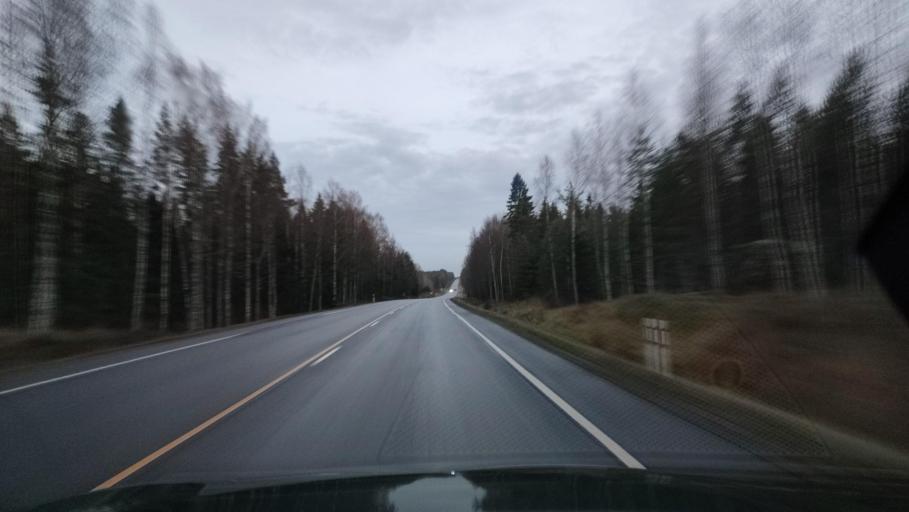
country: FI
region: Ostrobothnia
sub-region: Vaasa
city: Ristinummi
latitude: 62.9768
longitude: 21.7691
